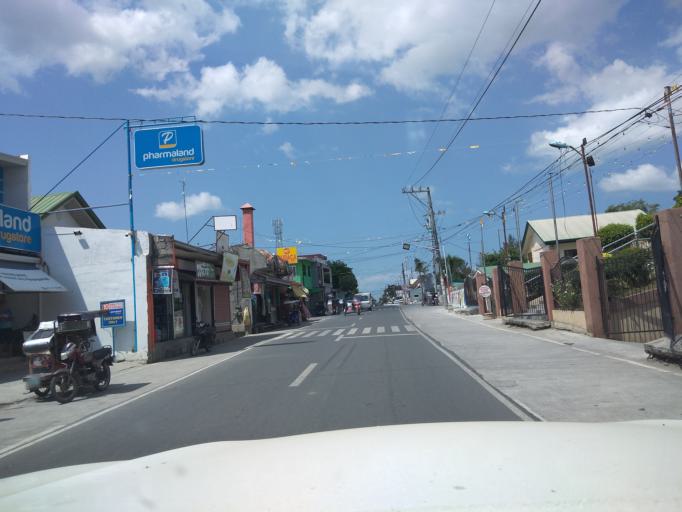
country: PH
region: Central Luzon
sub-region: Province of Pampanga
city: Bahay Pare
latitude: 15.0302
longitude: 120.8818
